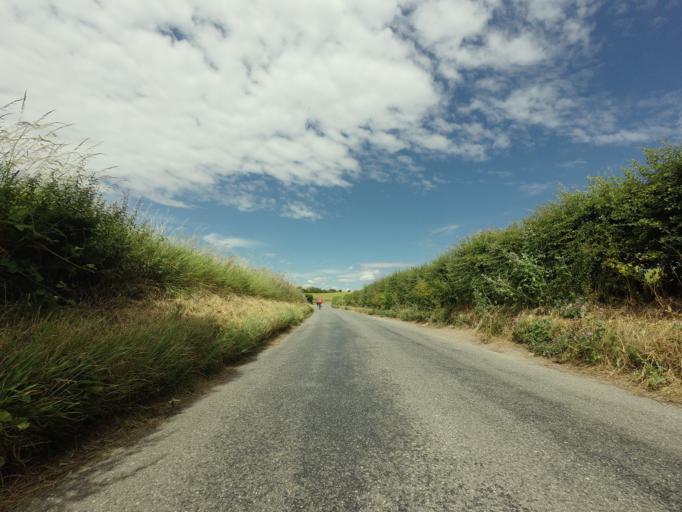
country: GB
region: England
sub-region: Kent
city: Strood
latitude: 51.4270
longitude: 0.4736
